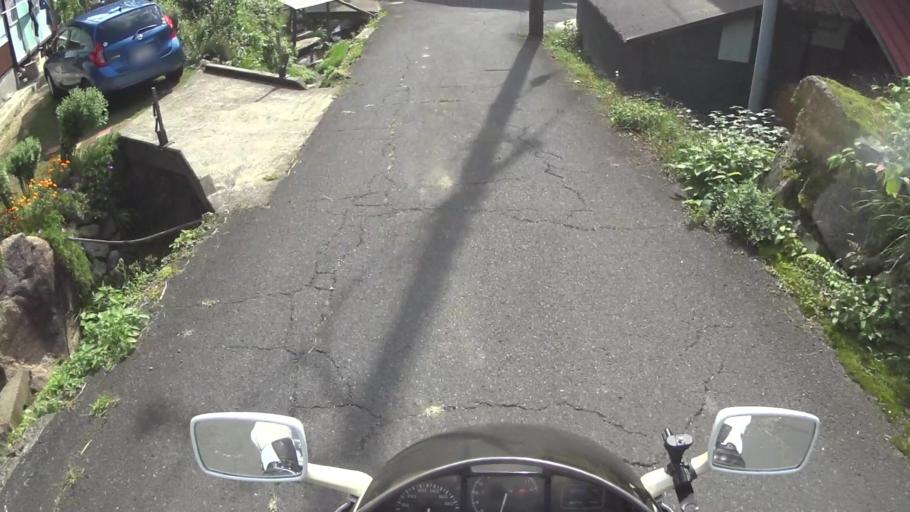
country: JP
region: Kyoto
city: Miyazu
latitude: 35.6112
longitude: 135.1962
